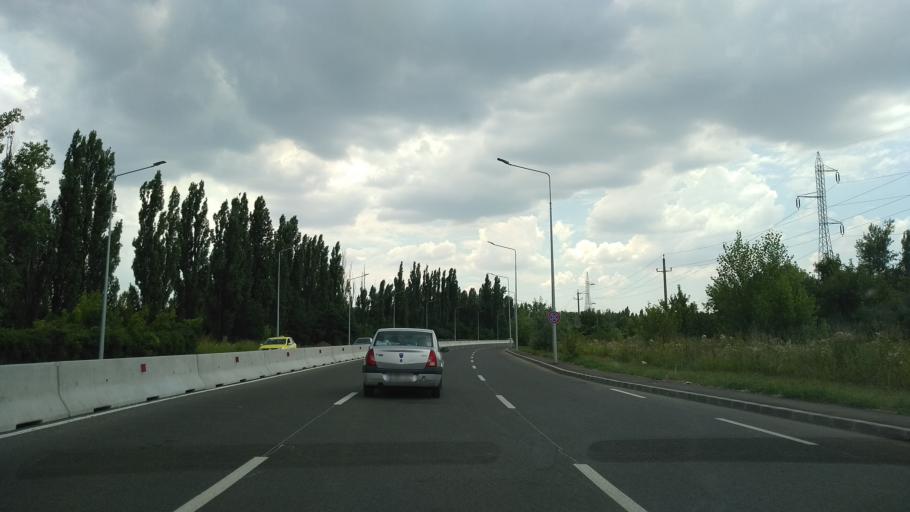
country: RO
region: Ilfov
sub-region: Comuna Popesti-Leordeni
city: Popesti-Leordeni
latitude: 44.3958
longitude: 26.1579
